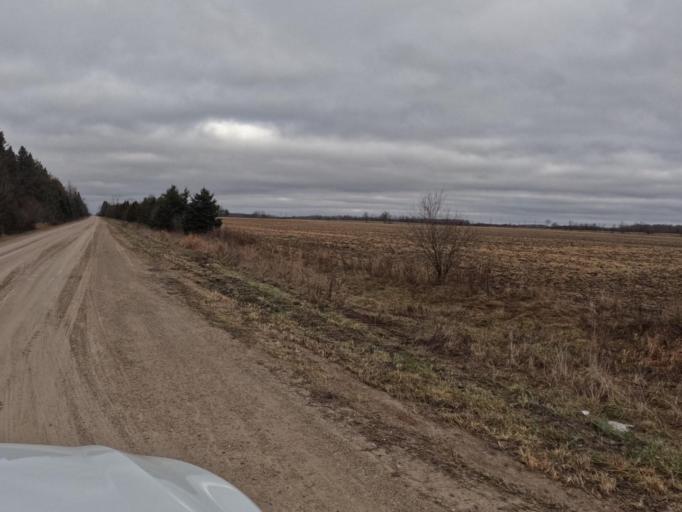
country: CA
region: Ontario
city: Shelburne
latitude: 43.9580
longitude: -80.3985
